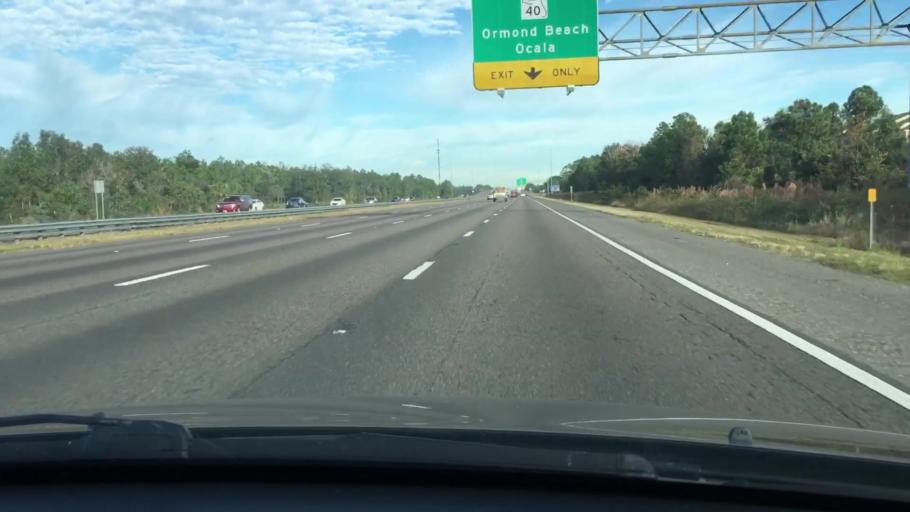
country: US
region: Florida
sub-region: Volusia County
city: Ormond Beach
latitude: 29.2474
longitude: -81.1125
